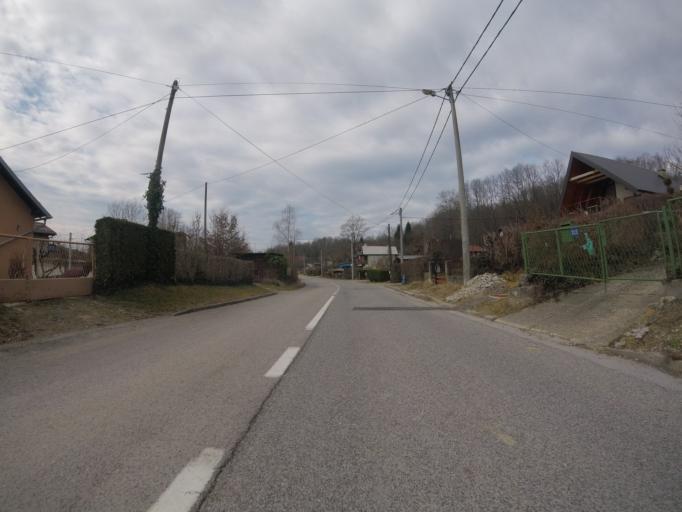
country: HR
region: Sisacko-Moslavacka
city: Glina
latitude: 45.4901
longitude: 16.0182
